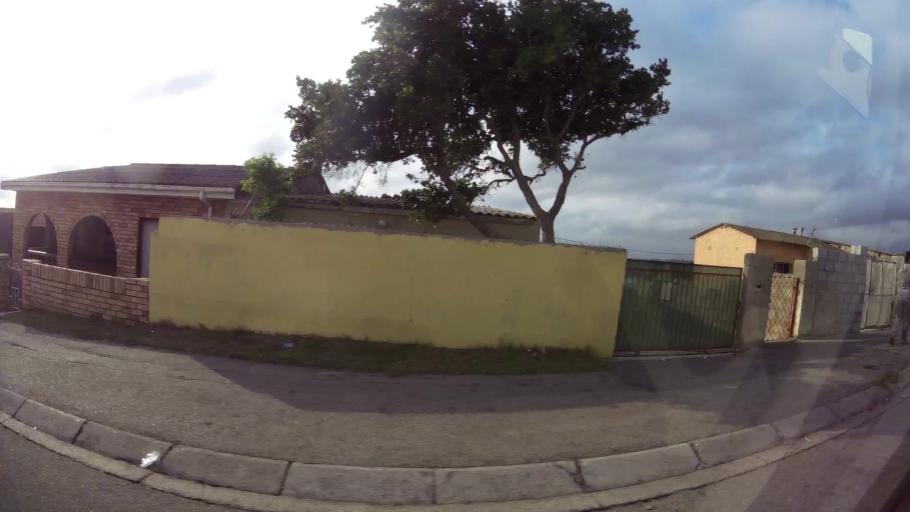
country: ZA
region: Eastern Cape
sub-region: Nelson Mandela Bay Metropolitan Municipality
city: Port Elizabeth
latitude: -33.9181
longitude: 25.5471
